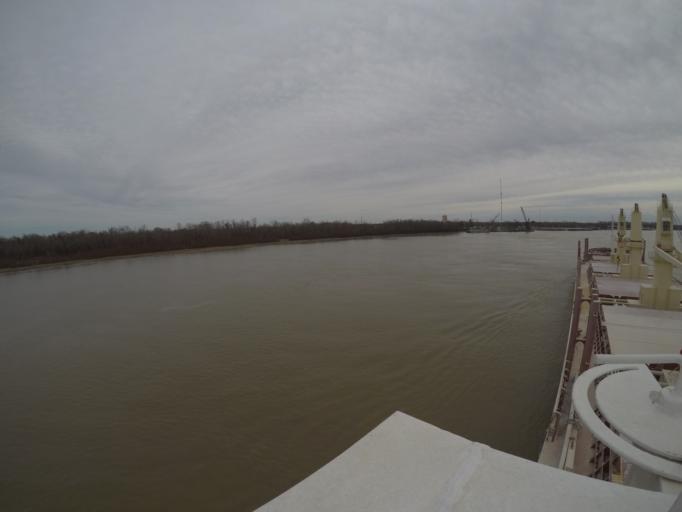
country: US
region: Louisiana
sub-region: Saint John the Baptist Parish
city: Laplace
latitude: 30.0513
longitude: -90.4842
